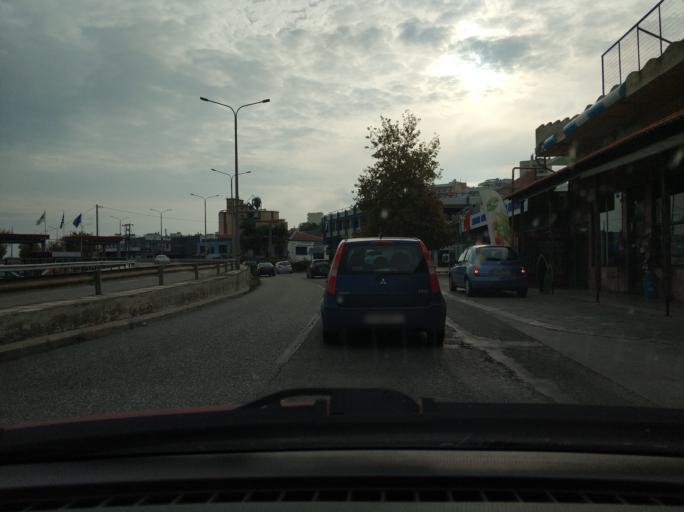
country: GR
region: East Macedonia and Thrace
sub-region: Nomos Kavalas
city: Kavala
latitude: 40.9287
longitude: 24.3907
